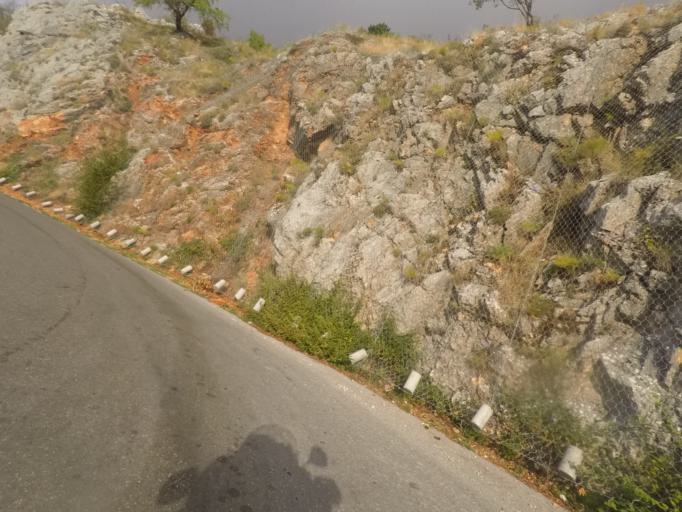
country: ME
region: Kotor
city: Kotor
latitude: 42.3990
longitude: 18.7837
